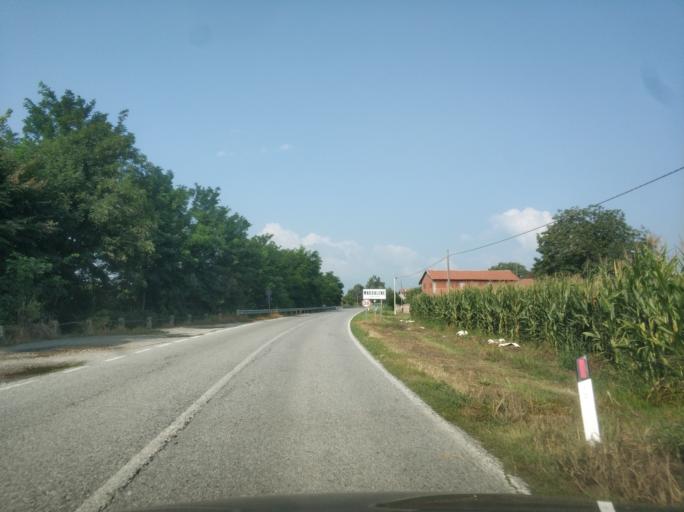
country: IT
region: Piedmont
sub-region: Provincia di Cuneo
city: Montanera
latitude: 44.5125
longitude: 7.6526
